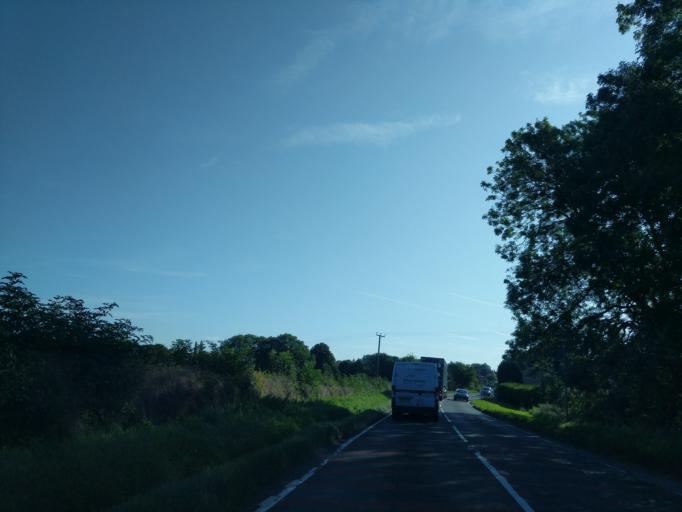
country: GB
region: England
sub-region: District of Rutland
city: Clipsham
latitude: 52.8117
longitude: -0.5264
